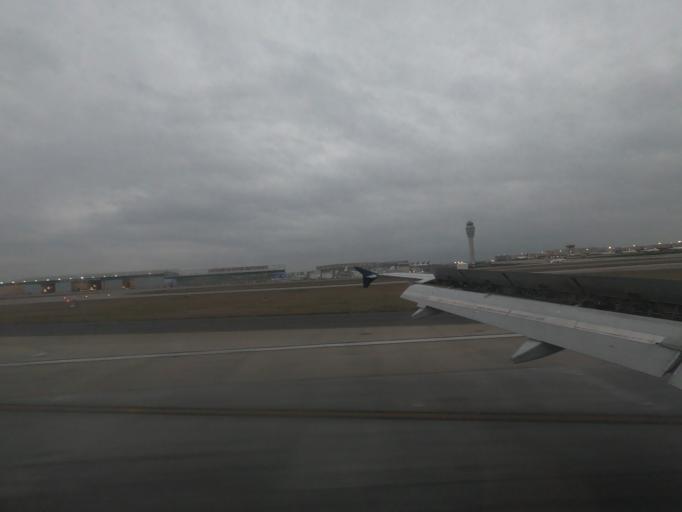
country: US
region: Georgia
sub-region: Fulton County
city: Hapeville
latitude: 33.6496
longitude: -84.4181
